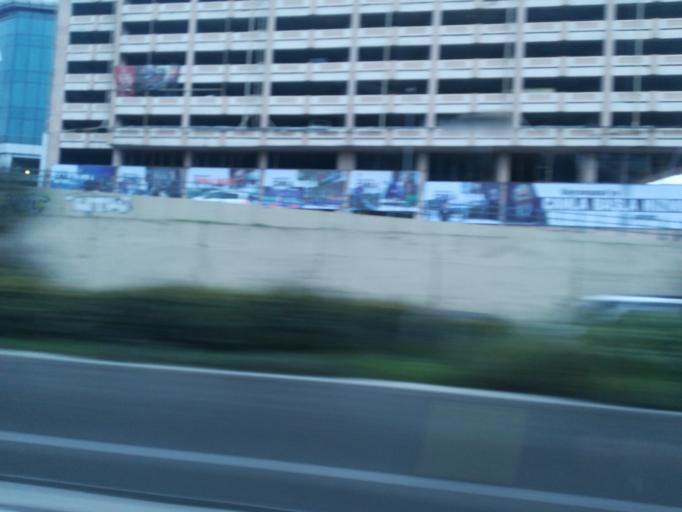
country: TR
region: Istanbul
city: Esenler
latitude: 41.0400
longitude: 28.9117
